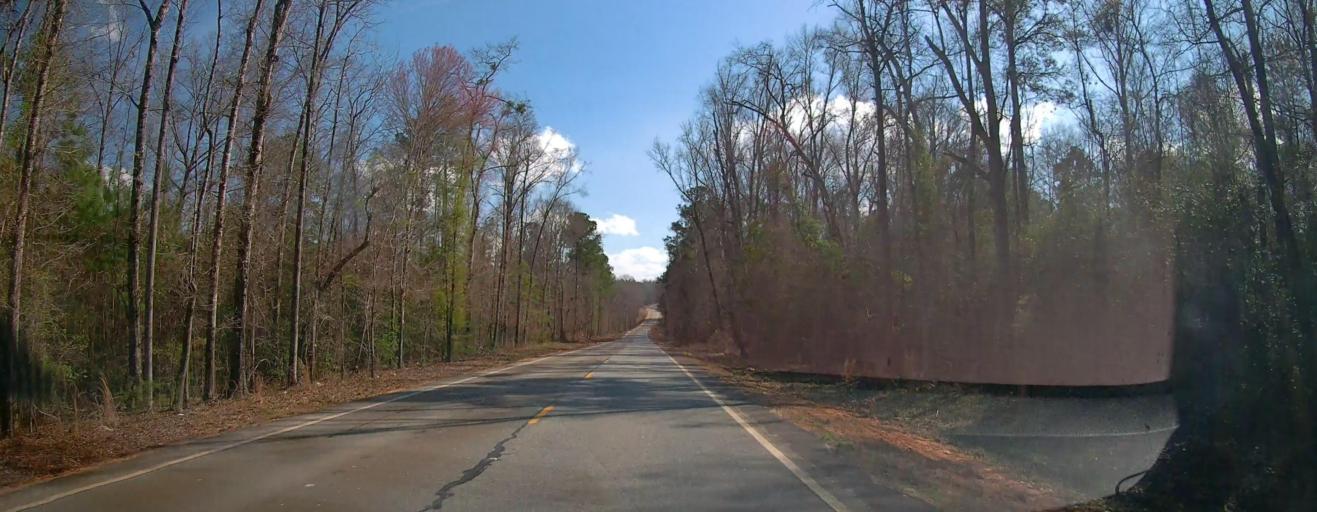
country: US
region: Georgia
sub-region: Wilkinson County
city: Gordon
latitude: 32.8194
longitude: -83.3248
